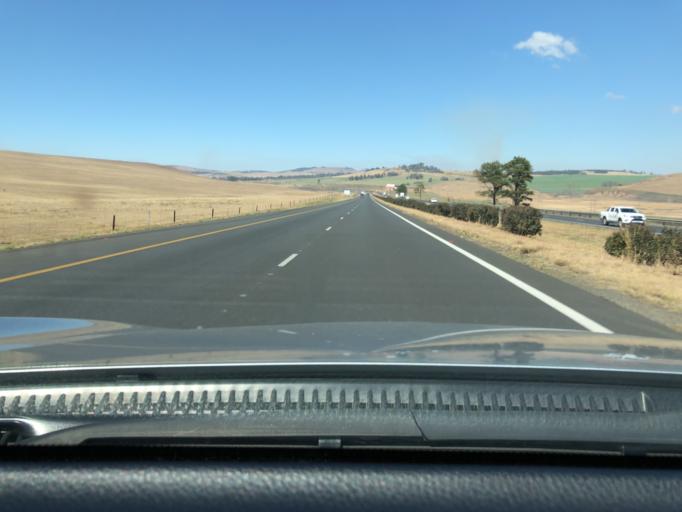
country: ZA
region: KwaZulu-Natal
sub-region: uMgungundlovu District Municipality
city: Mooirivier
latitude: -29.1709
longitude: 29.9840
